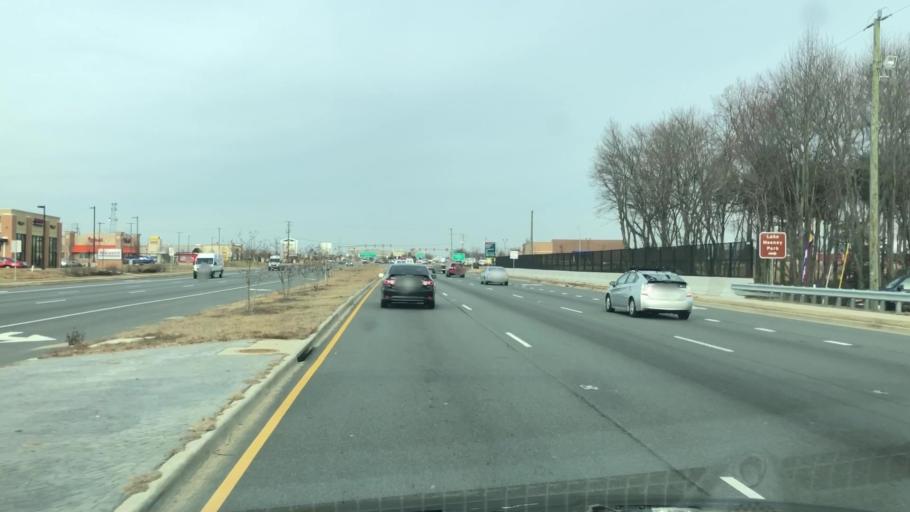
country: US
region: Virginia
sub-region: Stafford County
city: Falmouth
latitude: 38.3572
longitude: -77.5147
